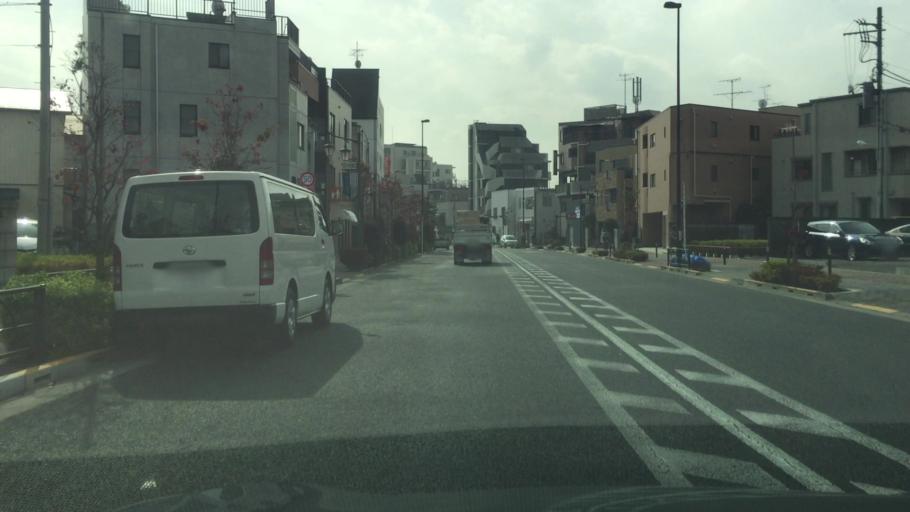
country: JP
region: Tokyo
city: Tokyo
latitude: 35.7431
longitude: 139.6889
